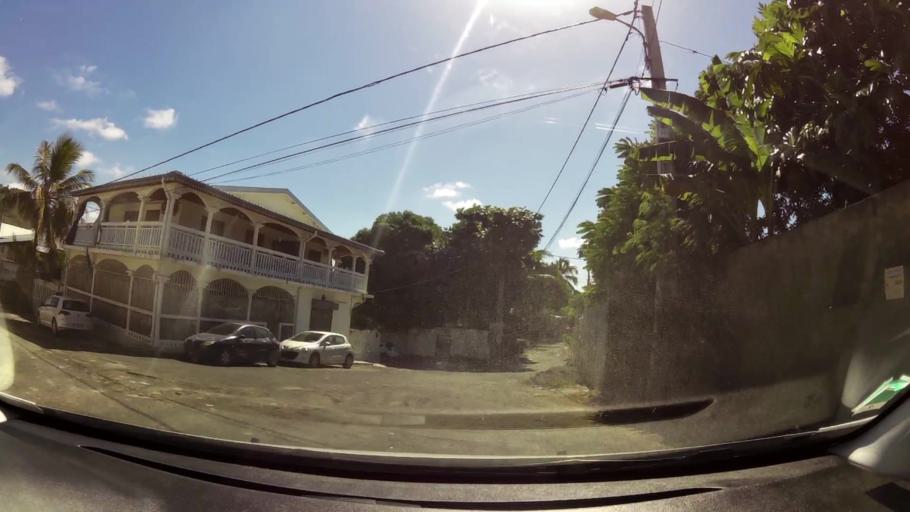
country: YT
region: Pamandzi
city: Pamandzi
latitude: -12.7913
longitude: 45.2823
